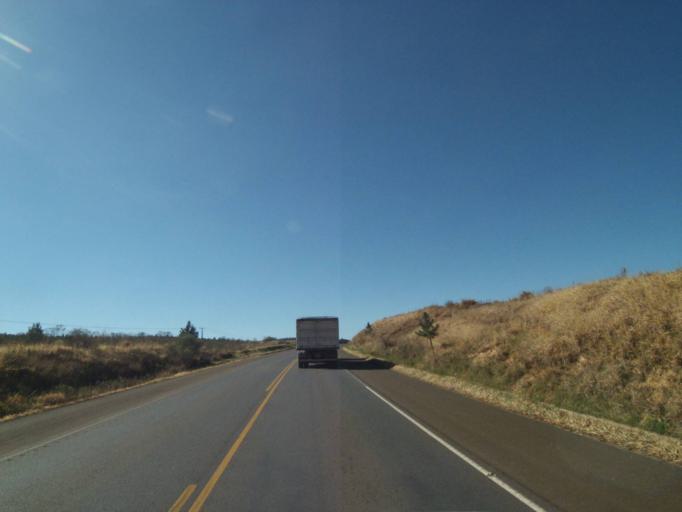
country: BR
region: Parana
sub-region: Tibagi
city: Tibagi
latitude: -24.4660
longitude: -50.4392
